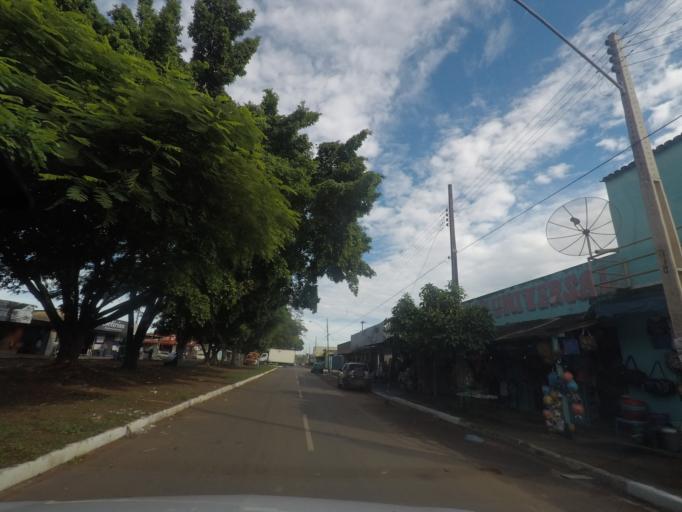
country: BR
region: Goias
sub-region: Aparecida De Goiania
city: Aparecida de Goiania
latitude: -16.8202
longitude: -49.3111
